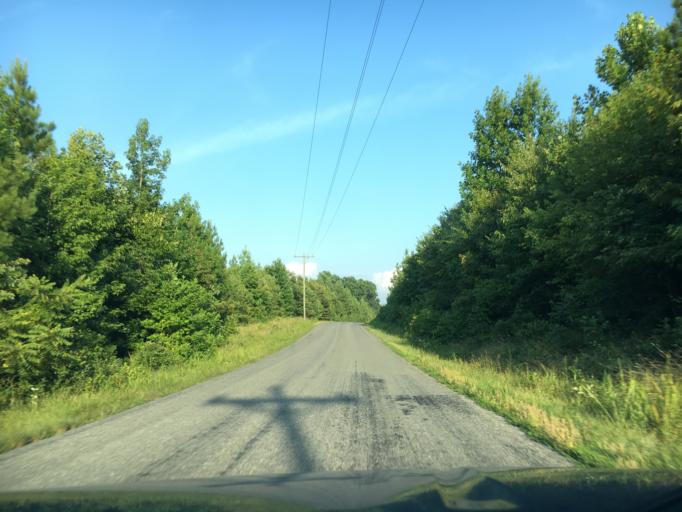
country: US
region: Virginia
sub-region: Pittsylvania County
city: Gretna
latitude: 36.8449
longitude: -79.2082
